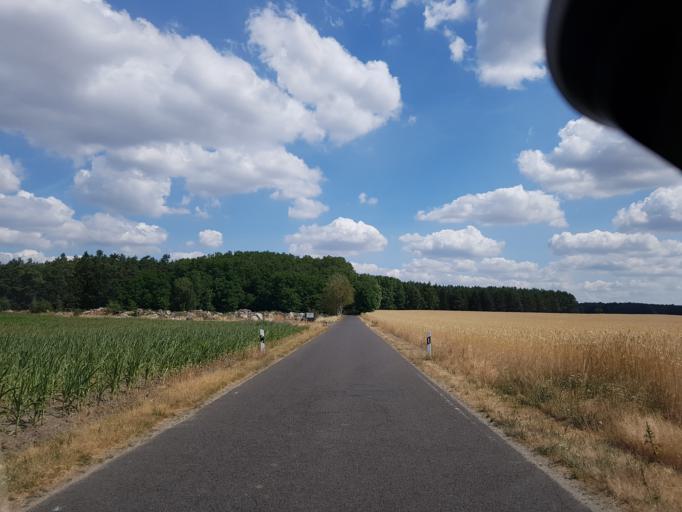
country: DE
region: Brandenburg
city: Drebkau
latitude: 51.6665
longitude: 14.2885
